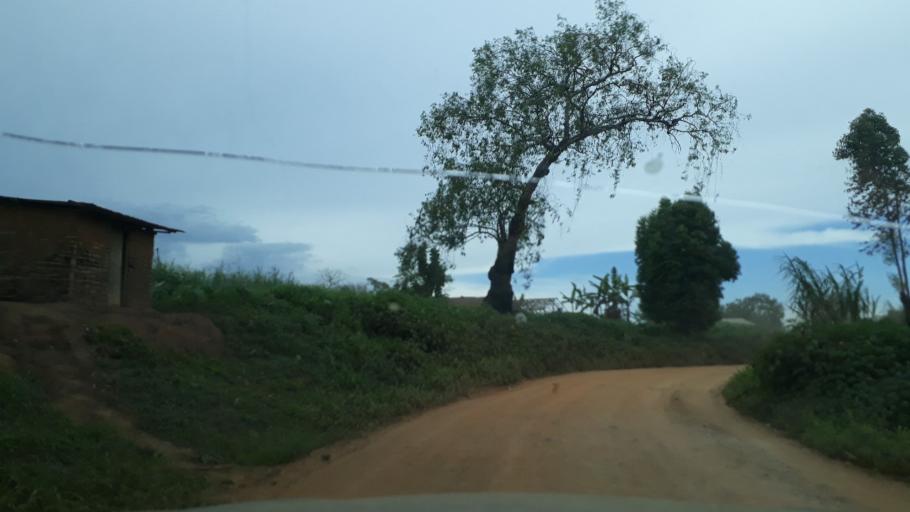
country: CD
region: Eastern Province
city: Bunia
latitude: 1.8956
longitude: 30.4899
